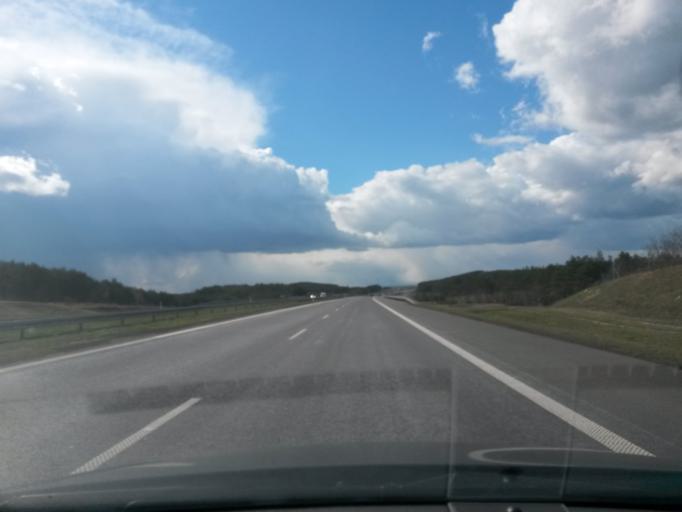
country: PL
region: Greater Poland Voivodeship
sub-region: Powiat kolski
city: Koscielec
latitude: 52.1416
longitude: 18.5448
